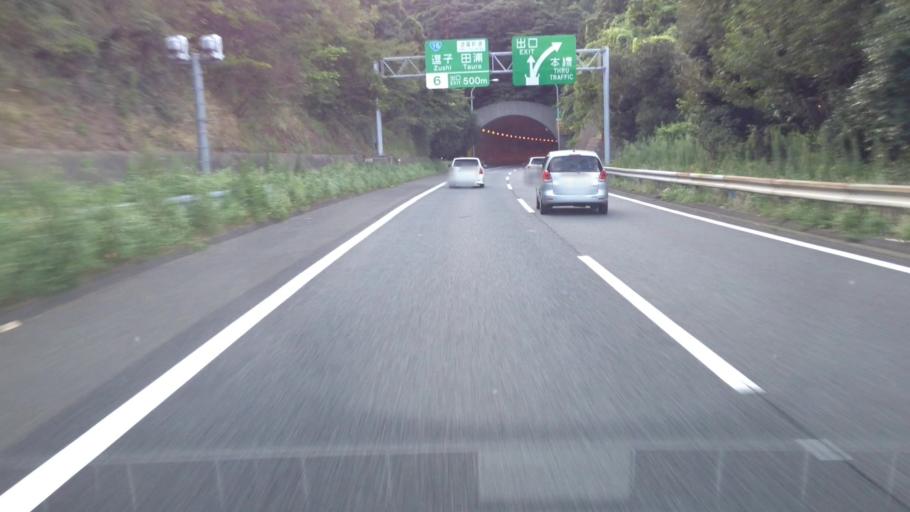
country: JP
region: Kanagawa
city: Yokosuka
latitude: 35.2839
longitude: 139.6245
